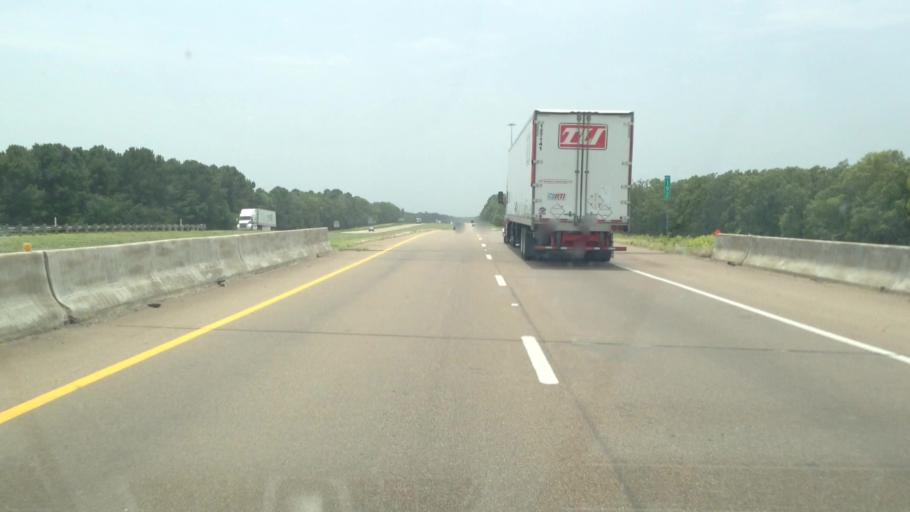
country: US
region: Texas
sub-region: Bowie County
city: De Kalb
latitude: 33.4152
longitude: -94.5588
